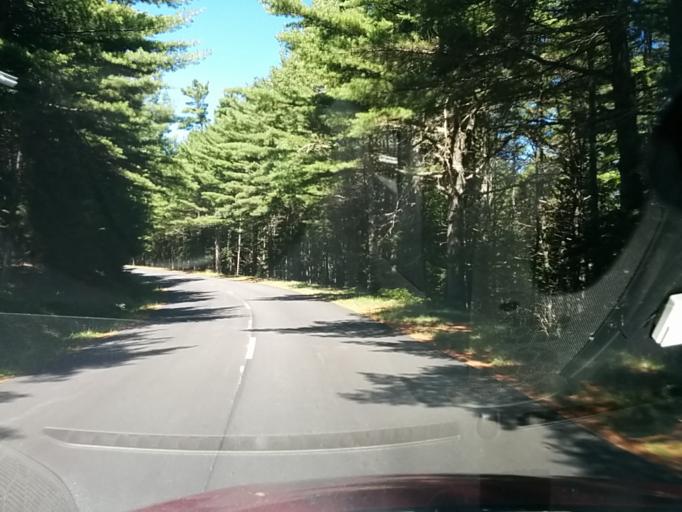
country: US
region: Maine
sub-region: Hancock County
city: Bar Harbor
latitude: 44.3169
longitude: -68.2273
